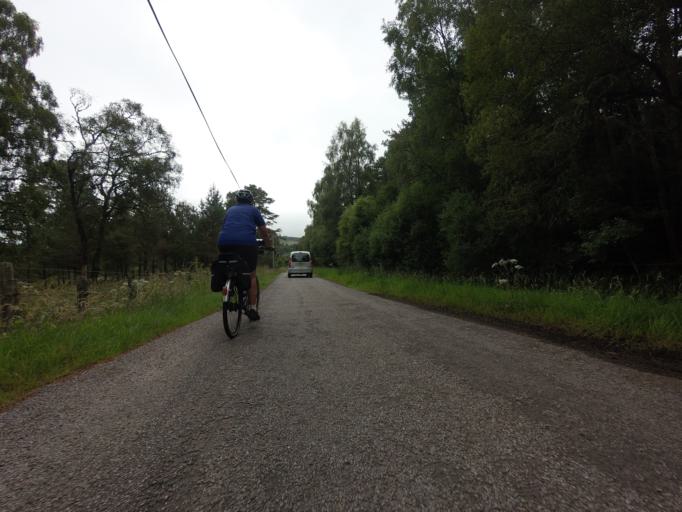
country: GB
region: Scotland
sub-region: Highland
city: Evanton
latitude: 57.9867
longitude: -4.4137
